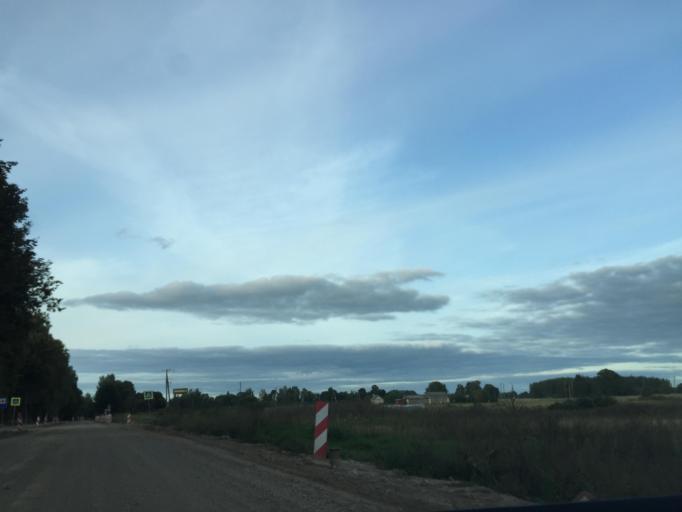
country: LV
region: Salas
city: Sala
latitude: 56.4033
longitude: 25.7685
